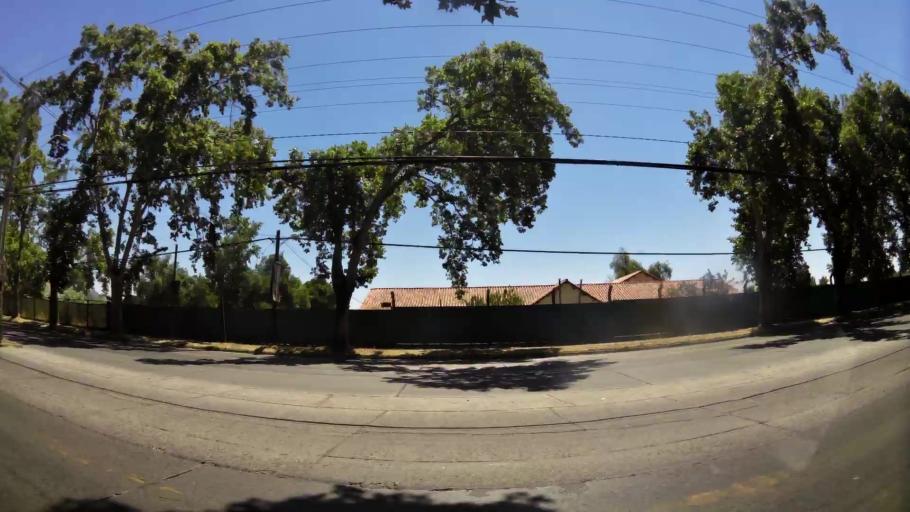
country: CL
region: Santiago Metropolitan
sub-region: Provincia de Maipo
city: San Bernardo
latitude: -33.5722
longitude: -70.6891
